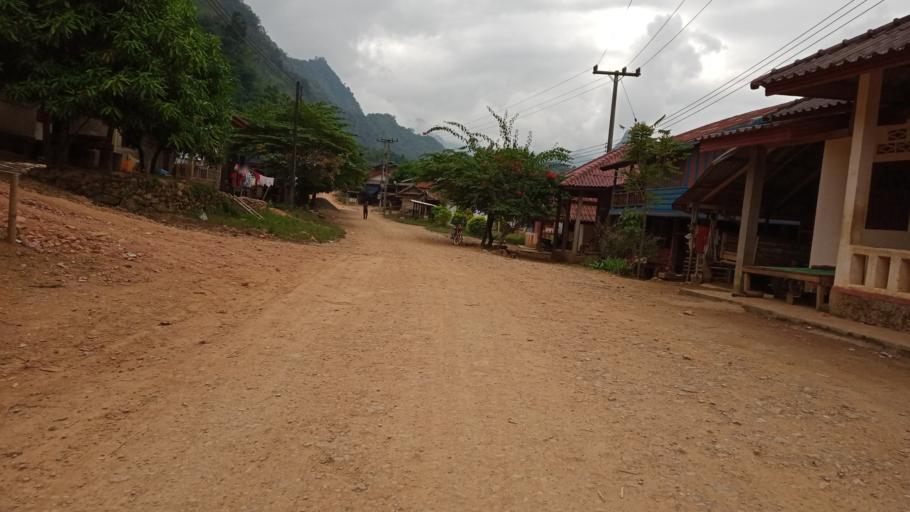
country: LA
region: Xiangkhoang
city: Phonsavan
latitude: 19.0928
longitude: 103.0011
